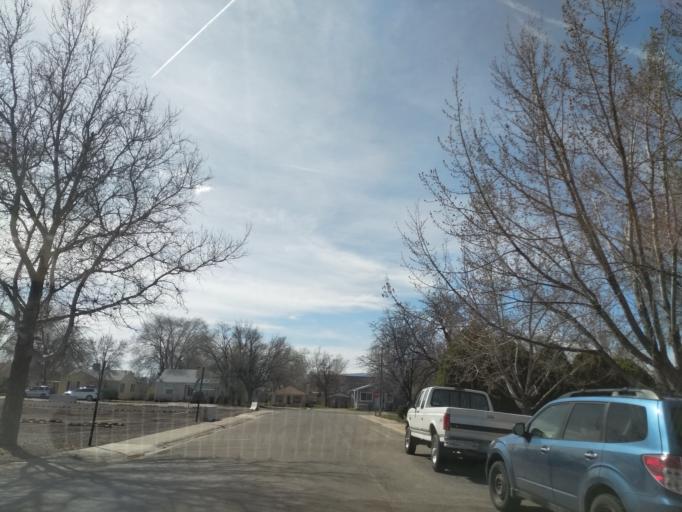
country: US
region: Colorado
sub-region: Mesa County
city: Grand Junction
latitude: 39.0826
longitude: -108.5596
